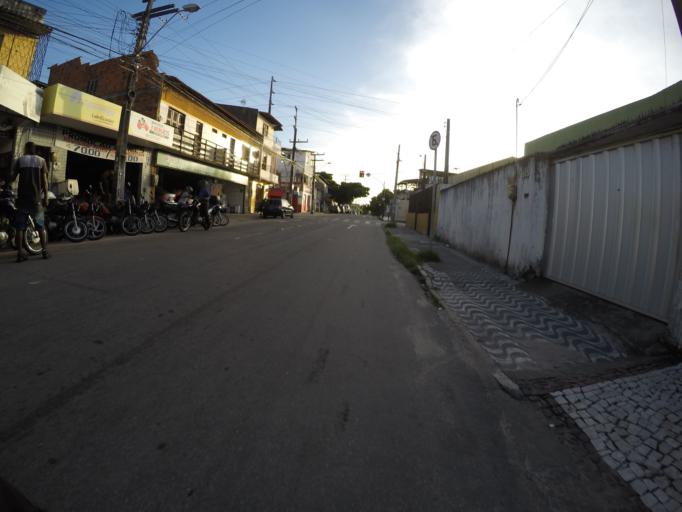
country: BR
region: Ceara
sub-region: Fortaleza
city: Fortaleza
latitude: -3.7559
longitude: -38.5129
